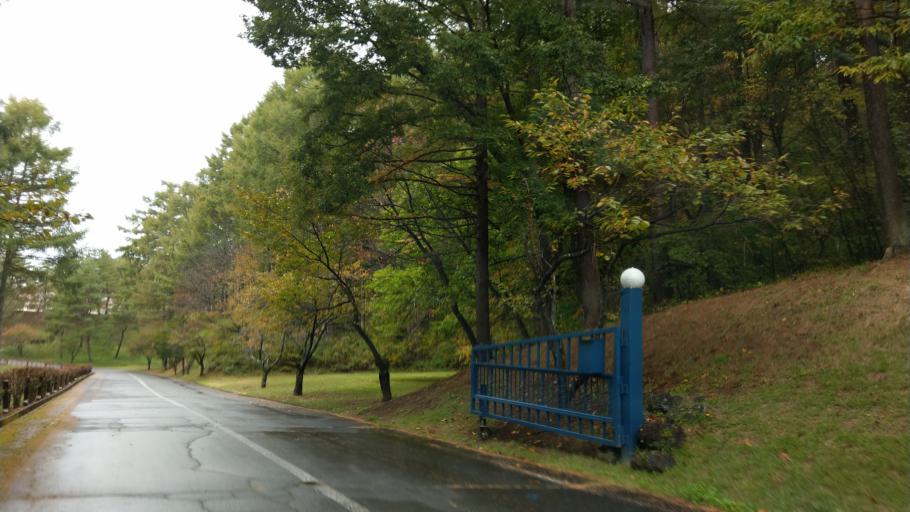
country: JP
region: Nagano
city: Komoro
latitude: 36.3667
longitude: 138.4269
